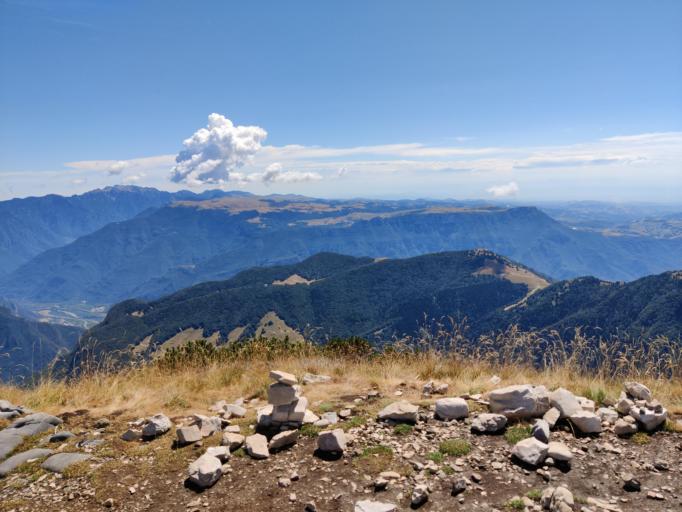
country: IT
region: Veneto
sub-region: Provincia di Verona
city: Malcesine
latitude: 45.7416
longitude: 10.8547
